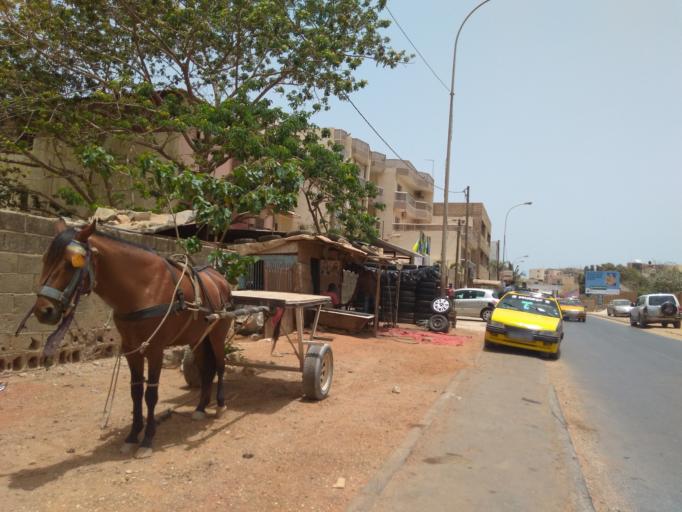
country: SN
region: Dakar
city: Grand Dakar
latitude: 14.7317
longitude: -17.4698
